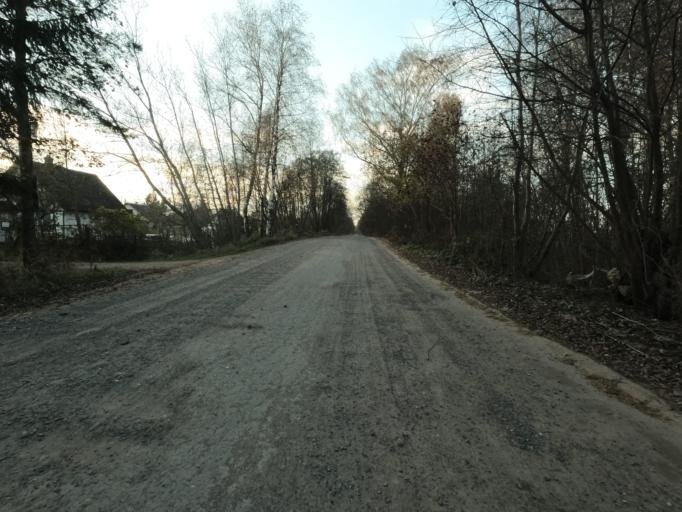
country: RU
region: Leningrad
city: Mga
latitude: 59.7667
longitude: 31.2407
